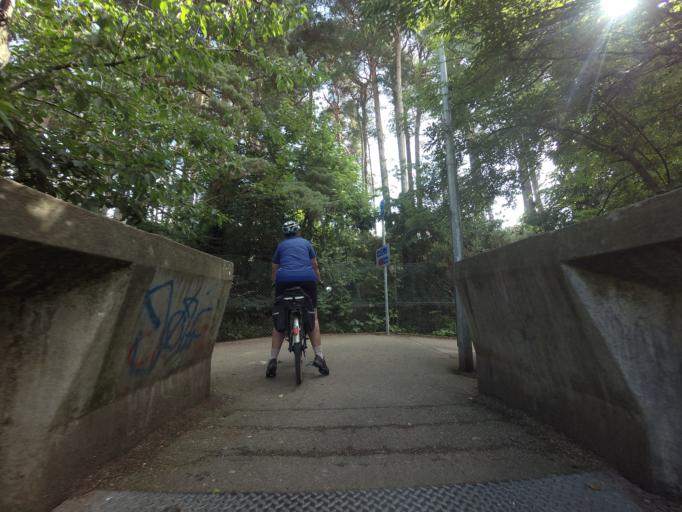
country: GB
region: Scotland
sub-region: Highland
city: Nairn
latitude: 57.5814
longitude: -3.8636
